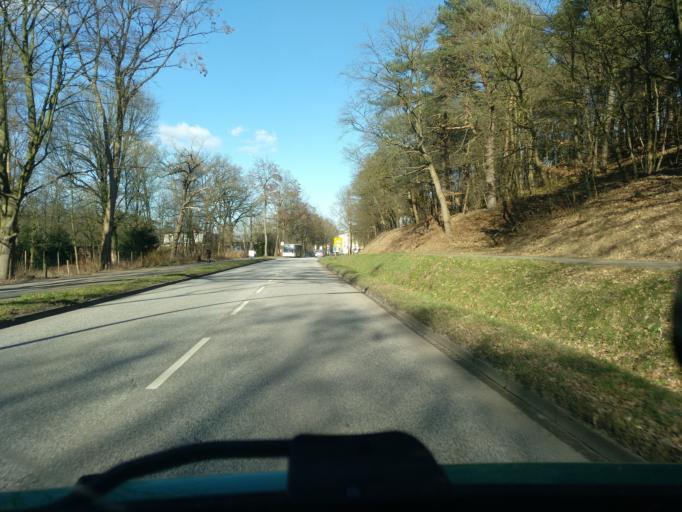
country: DE
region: Lower Saxony
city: Neu Wulmstorf
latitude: 53.4690
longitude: 9.8884
